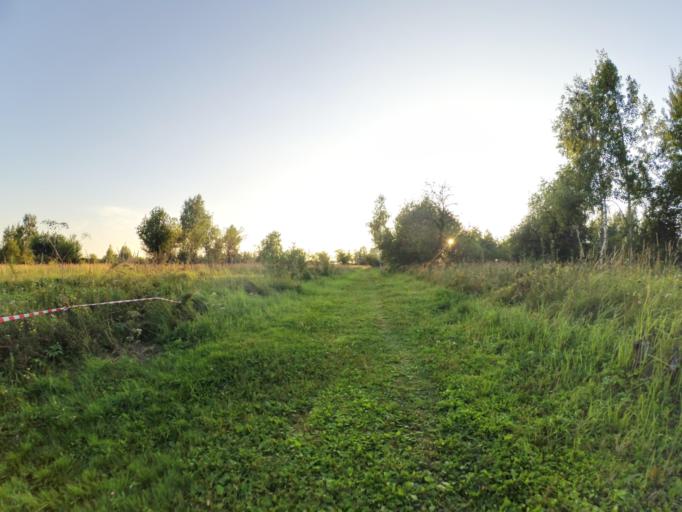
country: RU
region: Moscow
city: Strogino
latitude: 55.8589
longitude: 37.4020
